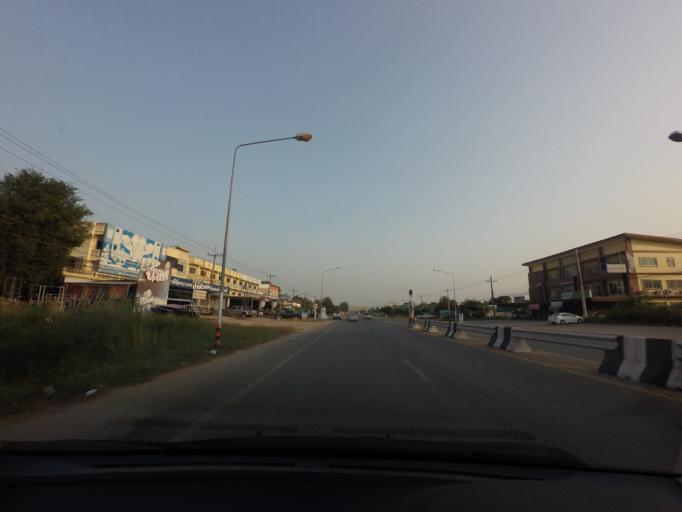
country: TH
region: Sukhothai
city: Sukhothai
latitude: 17.0176
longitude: 99.8303
